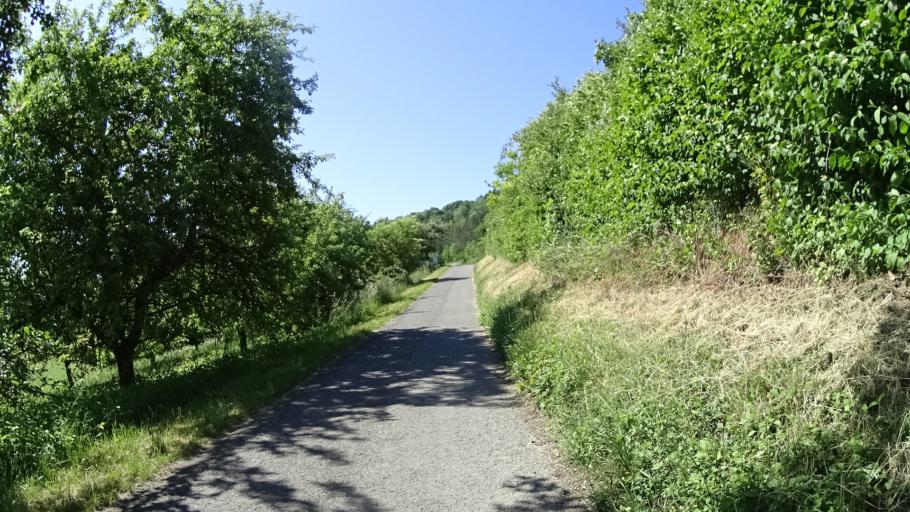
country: DE
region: Baden-Wuerttemberg
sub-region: Regierungsbezirk Stuttgart
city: Igersheim
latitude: 49.4835
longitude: 9.8150
